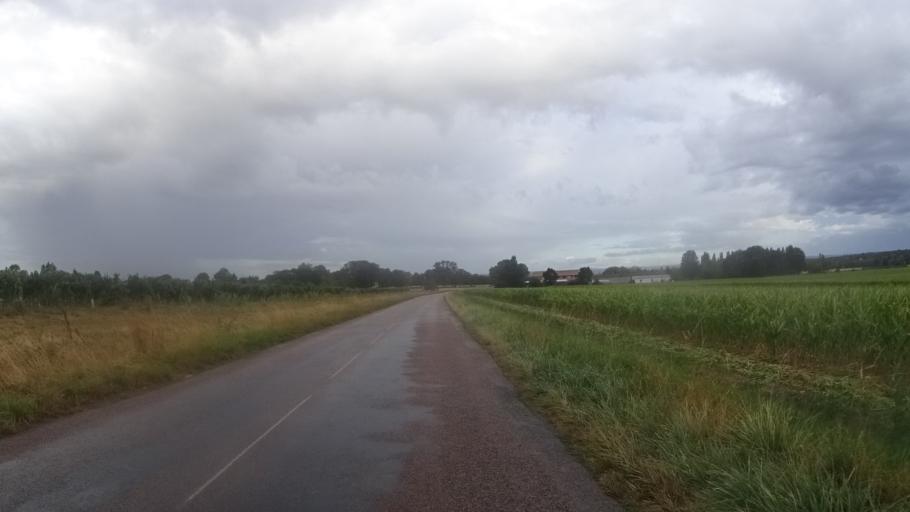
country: FR
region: Bourgogne
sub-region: Departement de Saone-et-Loire
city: Gergy
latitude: 46.9467
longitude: 4.9198
